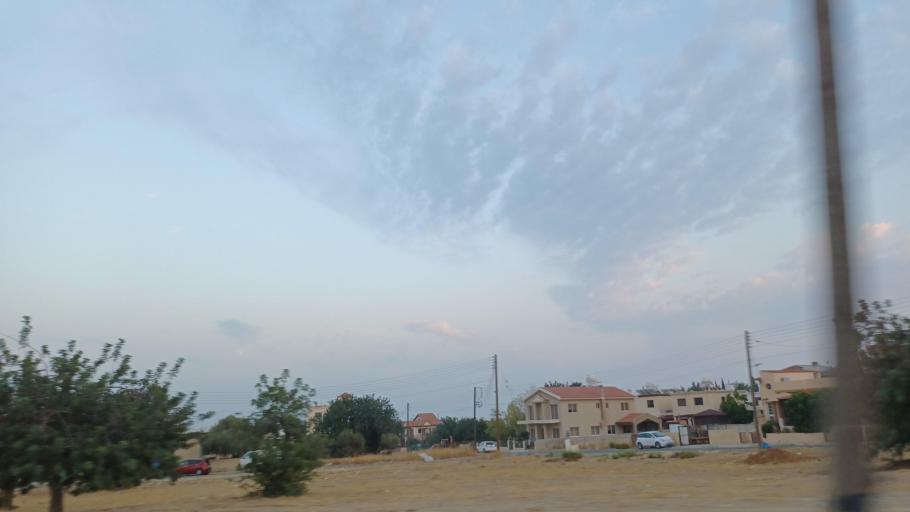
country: CY
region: Limassol
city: Ypsonas
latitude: 34.6983
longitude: 32.9675
